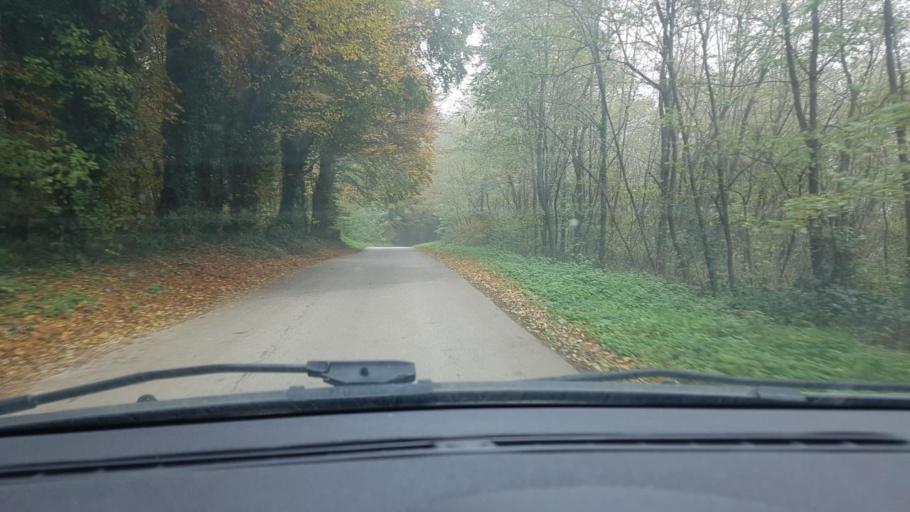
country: HR
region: Krapinsko-Zagorska
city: Mihovljan
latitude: 46.1445
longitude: 15.9781
